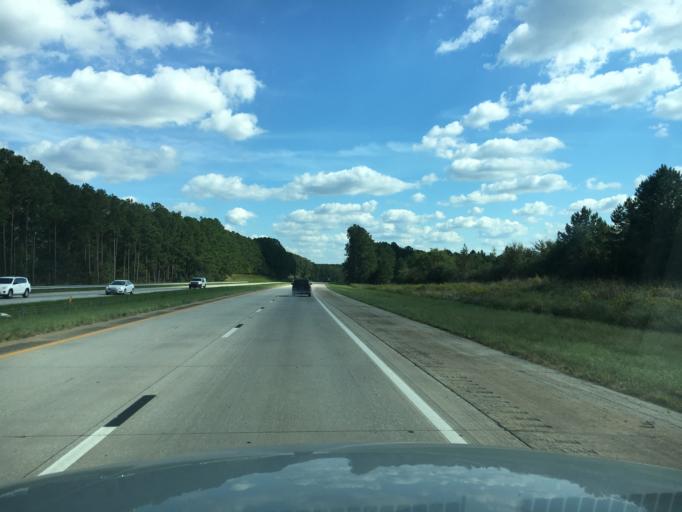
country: US
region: South Carolina
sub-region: Laurens County
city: Laurens
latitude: 34.6056
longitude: -82.0663
